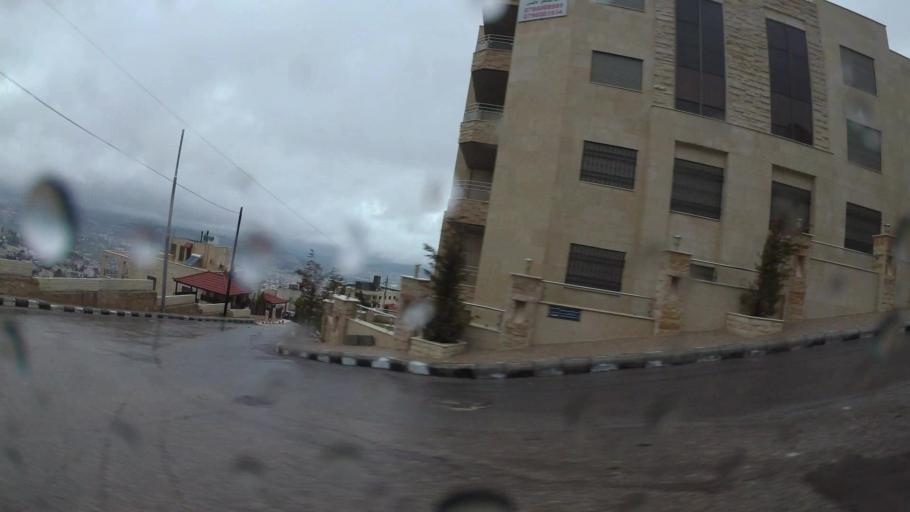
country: JO
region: Amman
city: Al Jubayhah
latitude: 32.0320
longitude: 35.8461
